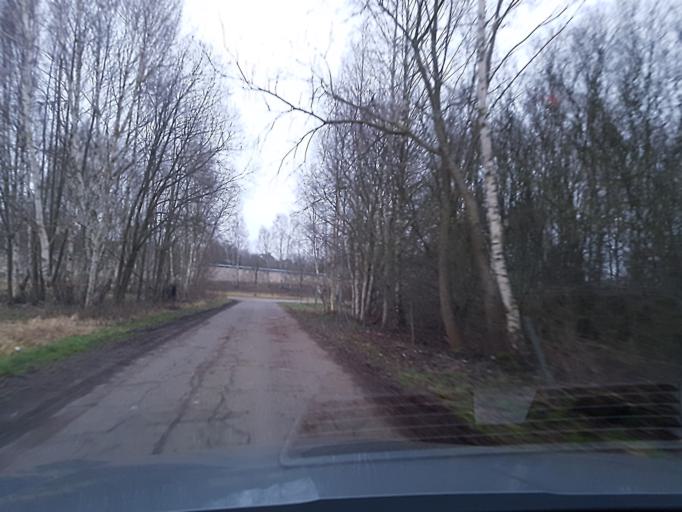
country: DE
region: Brandenburg
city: Doberlug-Kirchhain
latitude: 51.6308
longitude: 13.5867
